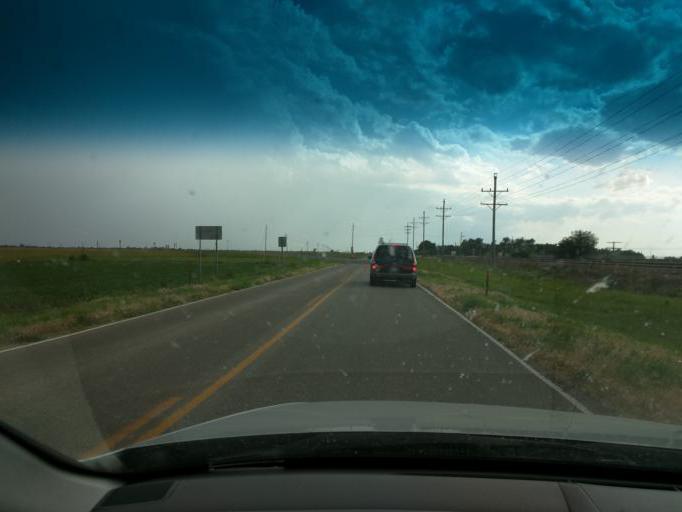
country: US
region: Kansas
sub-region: Reno County
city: South Hutchinson
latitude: 38.0148
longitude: -98.0007
